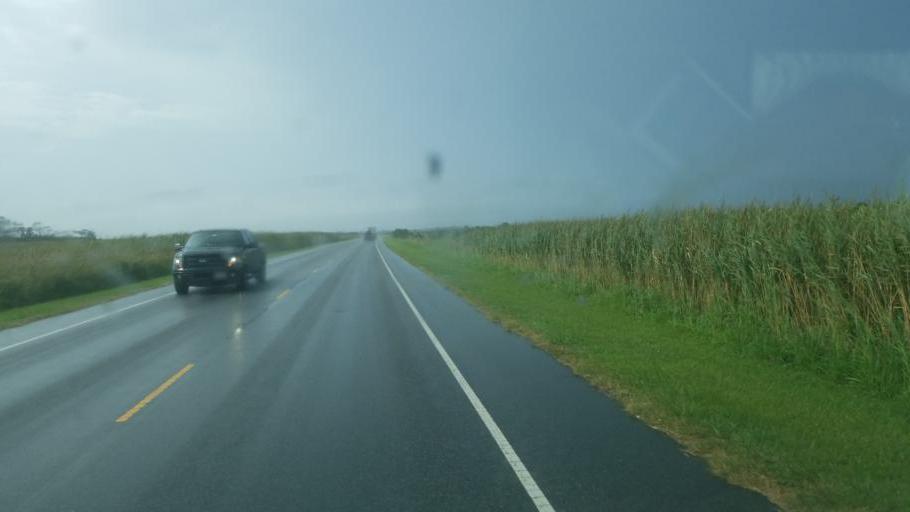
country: US
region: North Carolina
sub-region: Dare County
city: Wanchese
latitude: 35.8607
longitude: -75.5772
